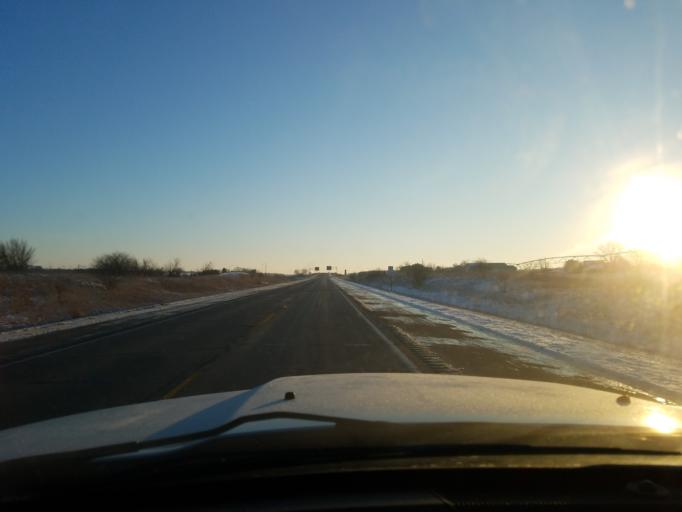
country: US
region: Indiana
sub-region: Marshall County
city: Bremen
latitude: 41.4607
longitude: -86.1671
